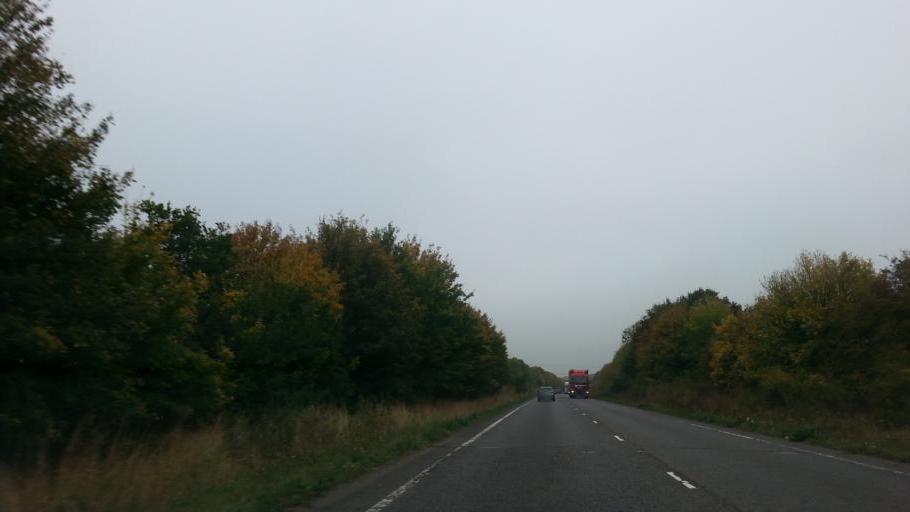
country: GB
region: England
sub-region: Peterborough
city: Castor
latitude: 52.5253
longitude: -0.3477
